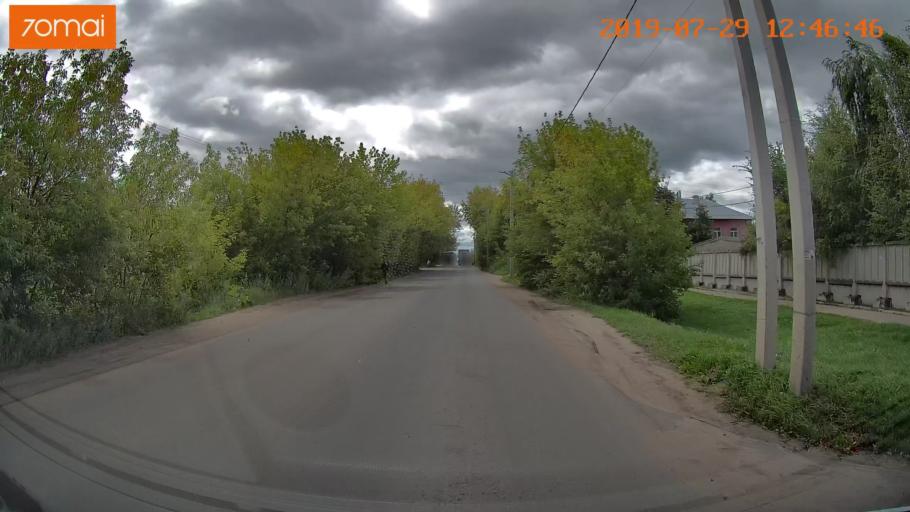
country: RU
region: Ivanovo
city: Novo-Talitsy
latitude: 56.9973
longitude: 40.9144
